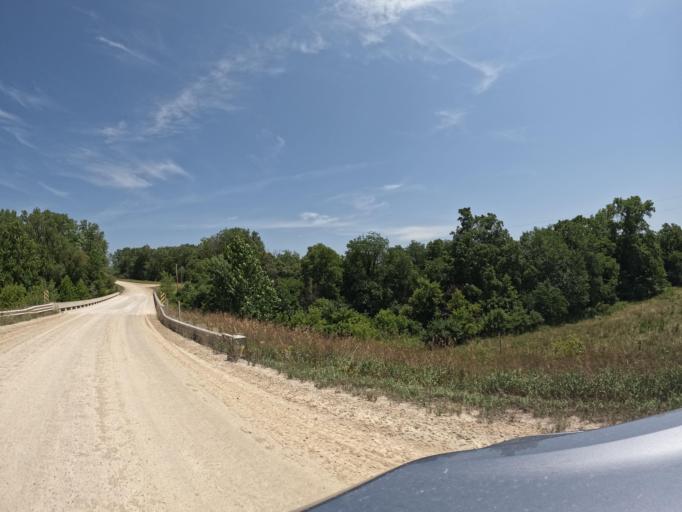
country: US
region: Iowa
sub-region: Henry County
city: Mount Pleasant
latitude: 40.9572
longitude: -91.5946
